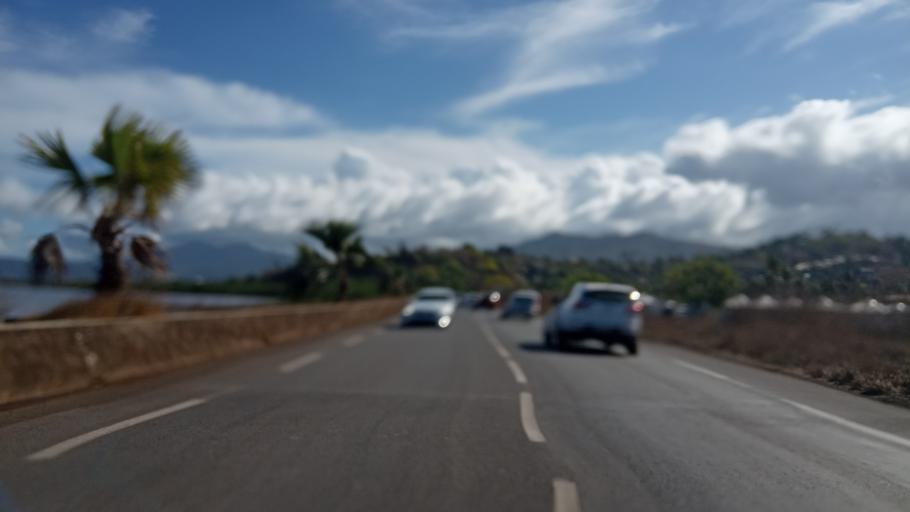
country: YT
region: Mamoudzou
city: Mamoudzou
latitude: -12.7936
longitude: 45.2192
